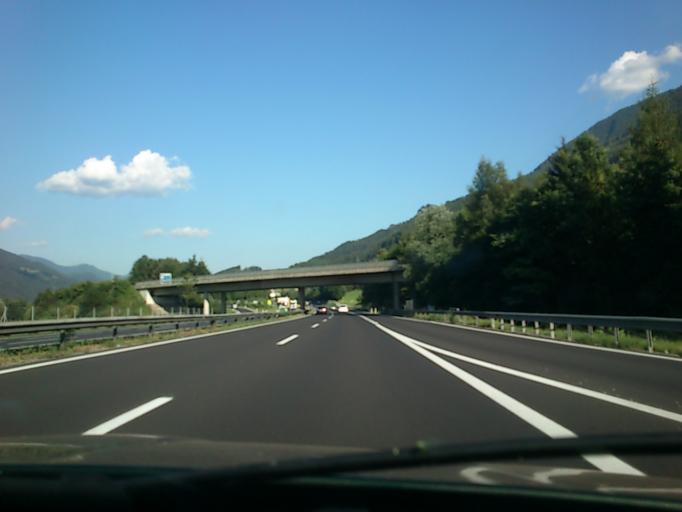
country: AT
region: Styria
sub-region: Politischer Bezirk Liezen
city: Rottenmann
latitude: 47.5258
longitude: 14.3346
